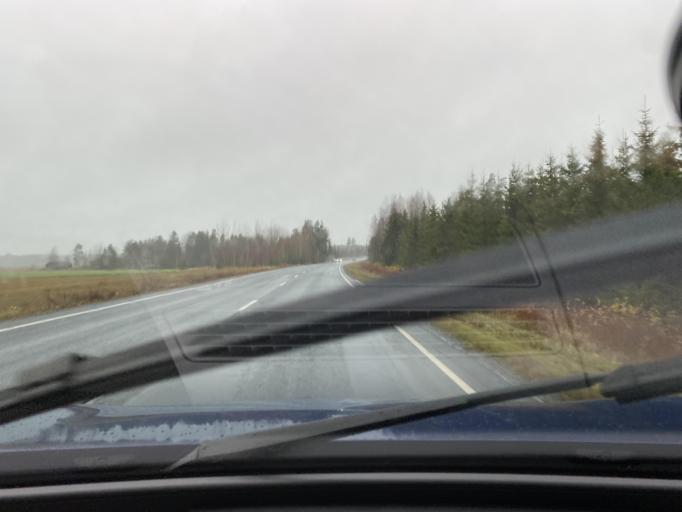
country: FI
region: Varsinais-Suomi
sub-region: Loimaa
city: Alastaro
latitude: 60.9094
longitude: 22.9150
